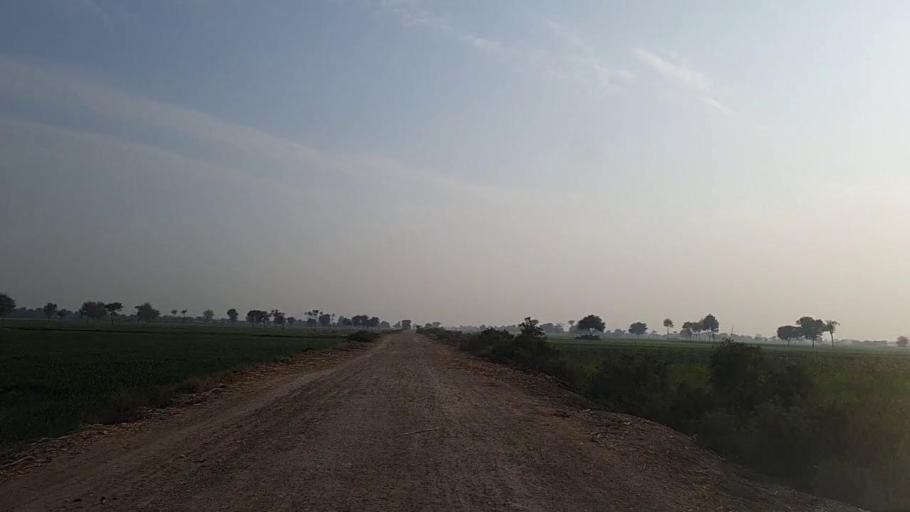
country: PK
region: Sindh
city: Jam Sahib
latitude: 26.3179
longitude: 68.5337
